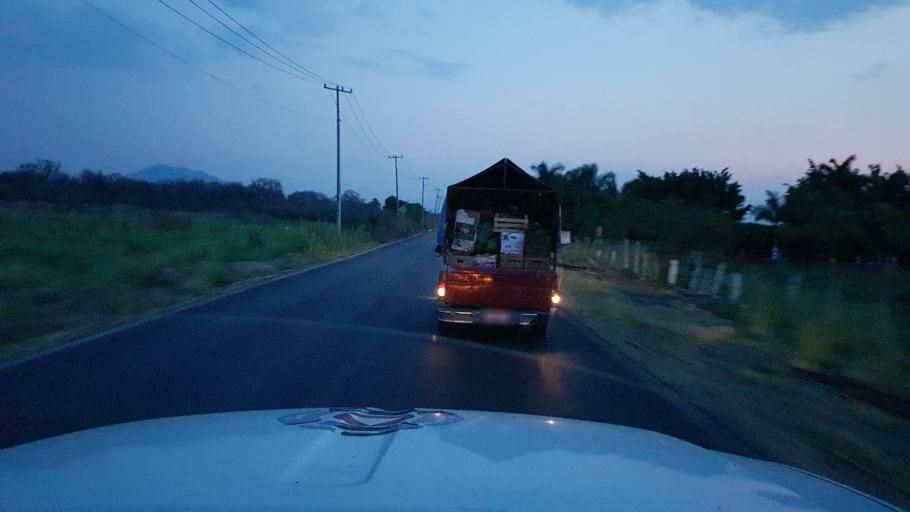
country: MX
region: Morelos
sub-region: Tlaquiltenango
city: Alfredo V. Bonfil (Chacampalco)
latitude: 18.6804
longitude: -99.1648
